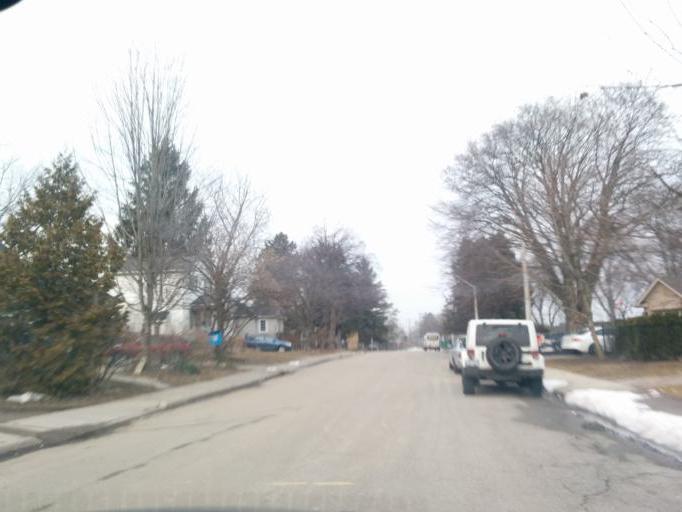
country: CA
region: Ontario
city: Mississauga
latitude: 43.5450
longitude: -79.5947
